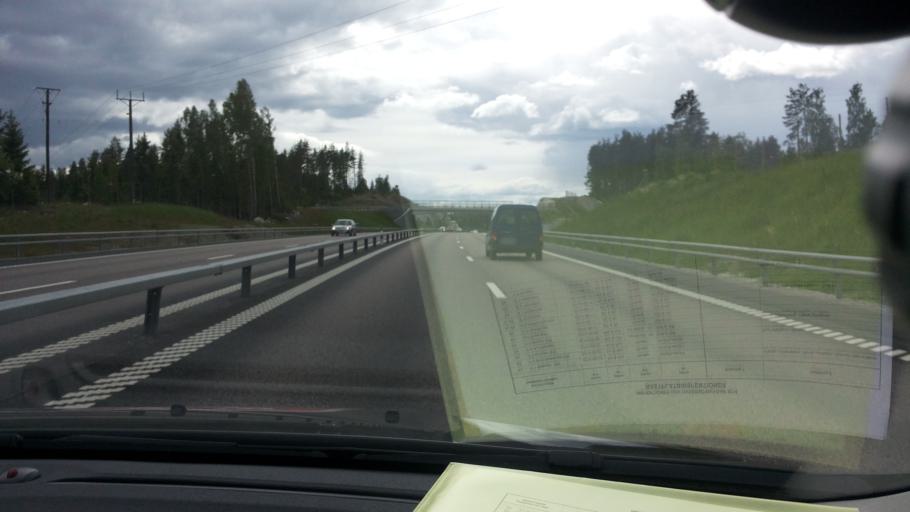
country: SE
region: Vaesternorrland
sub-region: Sundsvalls Kommun
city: Nolby
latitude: 62.2878
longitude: 17.3490
